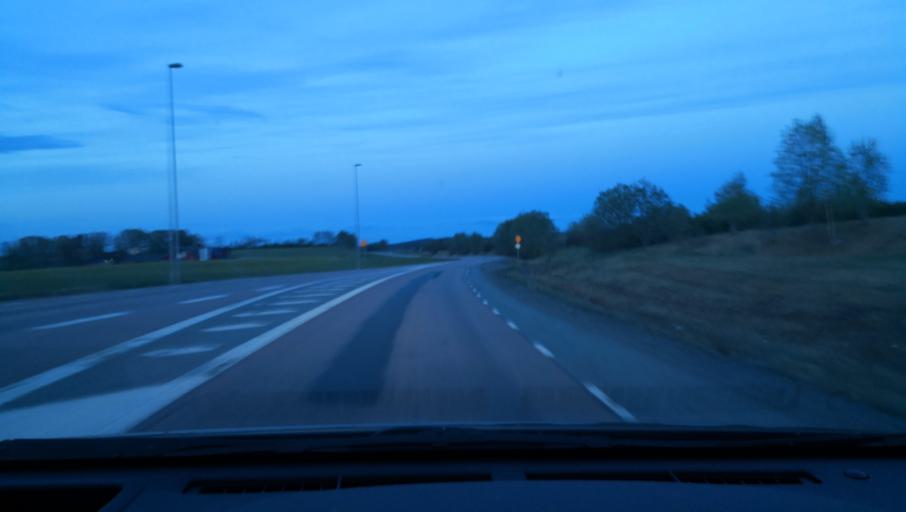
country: SE
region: OErebro
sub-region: Lekebergs Kommun
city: Fjugesta
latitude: 59.0361
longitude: 14.8741
